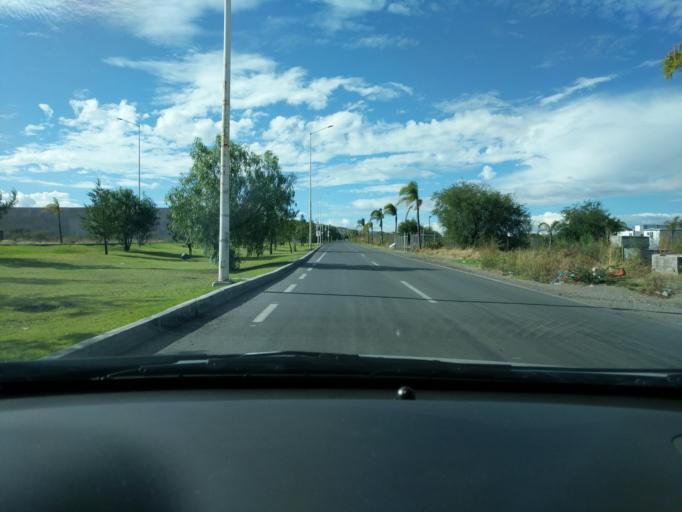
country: MX
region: Queretaro
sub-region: El Marques
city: Paseos del Marques
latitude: 20.5963
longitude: -100.2760
